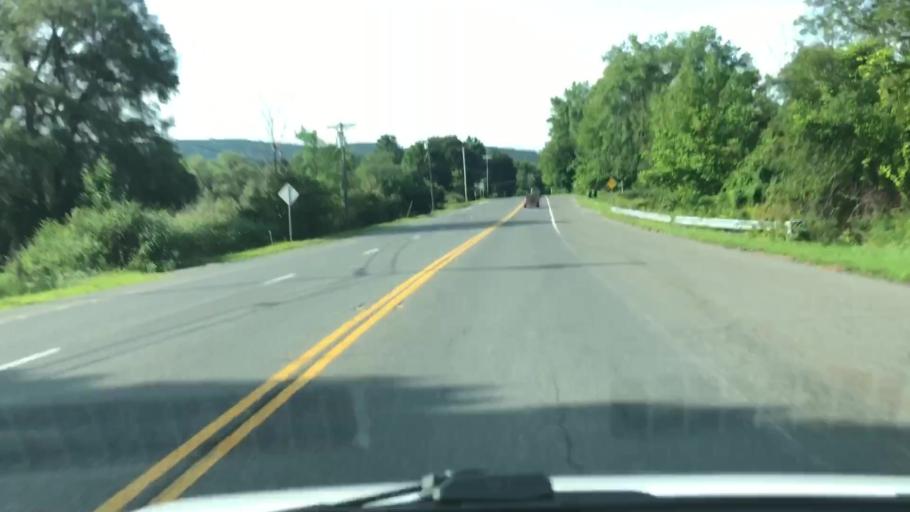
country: US
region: Massachusetts
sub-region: Berkshire County
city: Stockbridge
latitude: 42.2964
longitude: -73.2945
